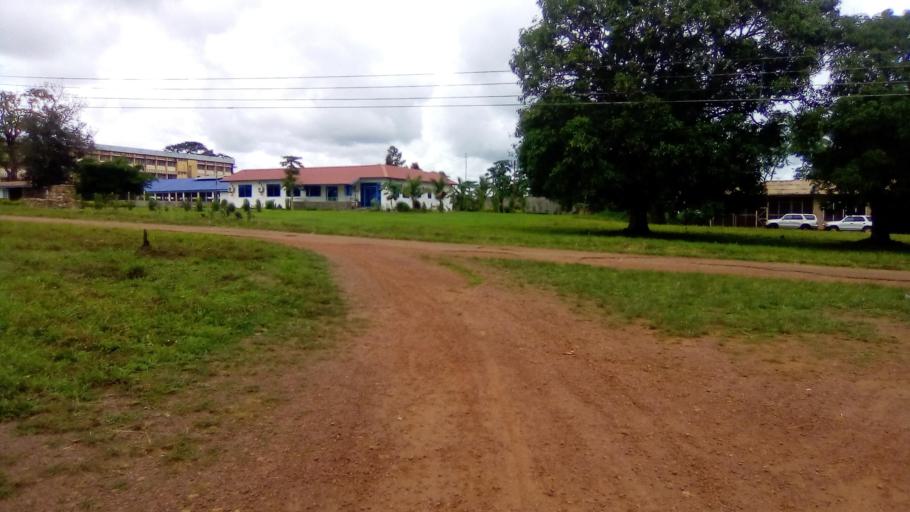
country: SL
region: Southern Province
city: Largo
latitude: 8.1181
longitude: -12.0704
